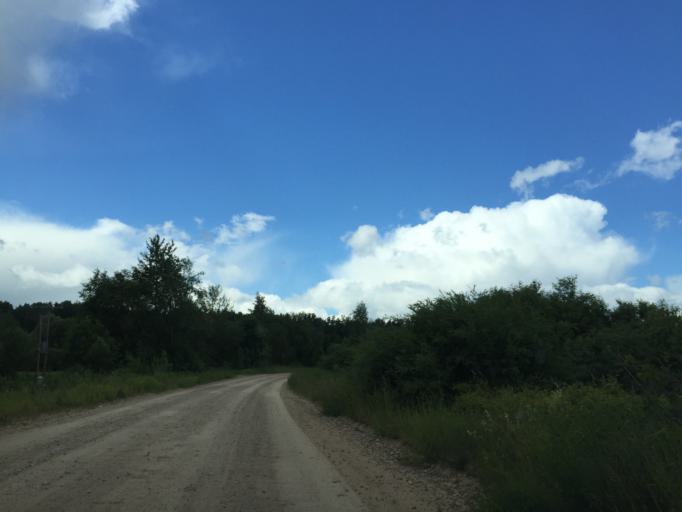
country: LV
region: Lecava
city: Iecava
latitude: 56.6223
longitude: 24.1822
